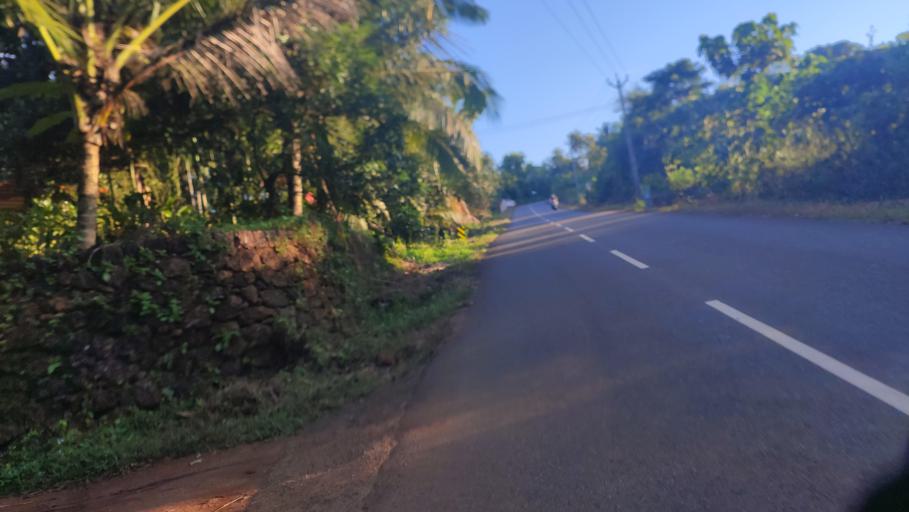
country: IN
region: Kerala
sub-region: Kasaragod District
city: Kasaragod
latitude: 12.4510
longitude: 75.0993
